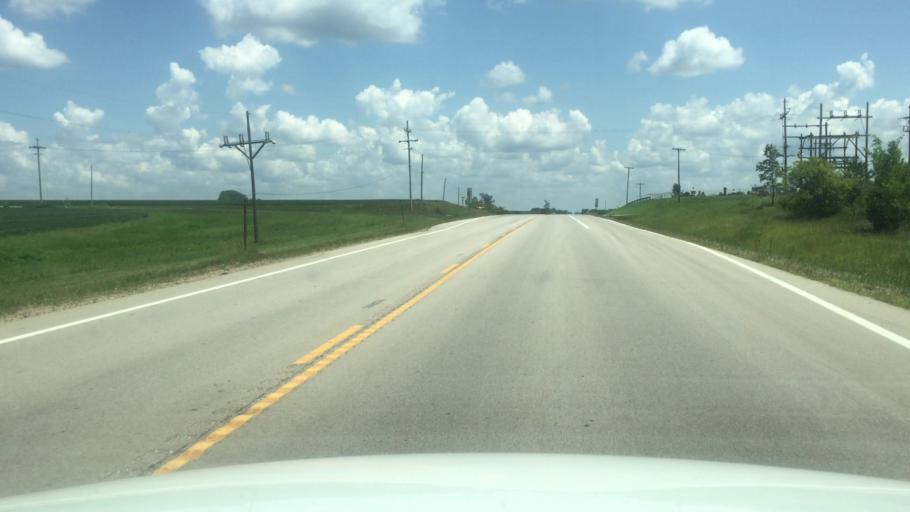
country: US
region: Kansas
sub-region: Brown County
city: Horton
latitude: 39.6674
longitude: -95.4914
